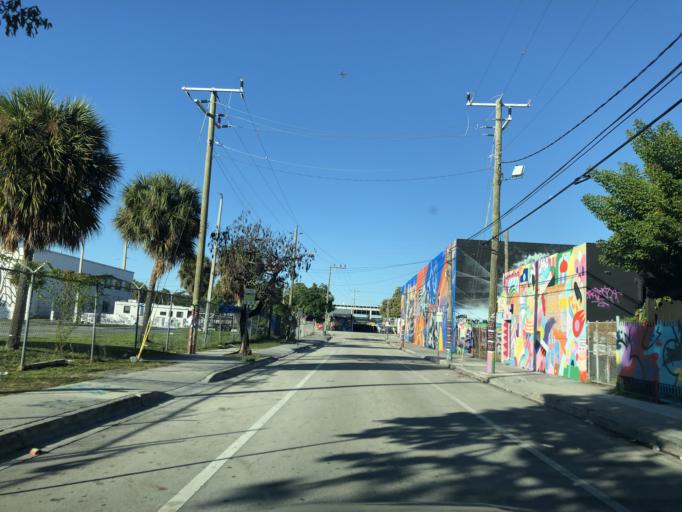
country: US
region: Florida
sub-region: Miami-Dade County
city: Miami
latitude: 25.7994
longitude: -80.2018
